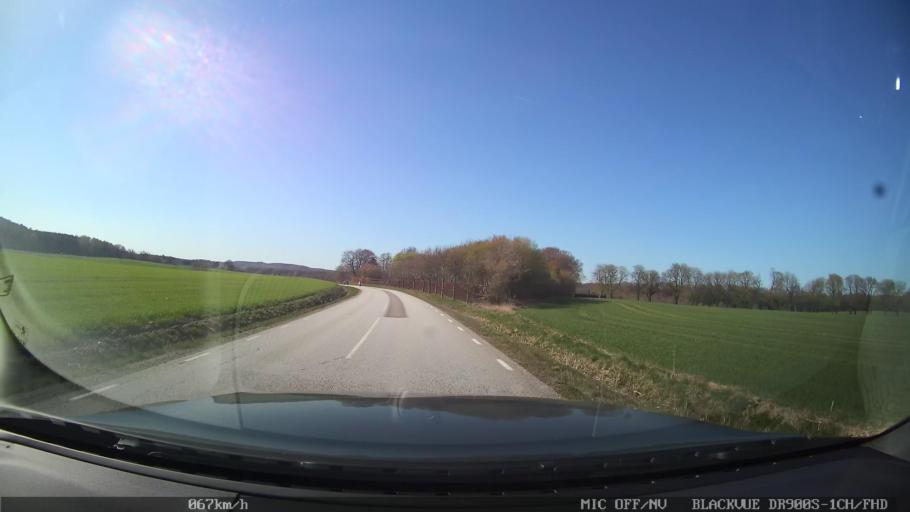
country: SE
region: Skane
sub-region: Klippans Kommun
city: Ljungbyhed
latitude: 55.9756
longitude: 13.2037
